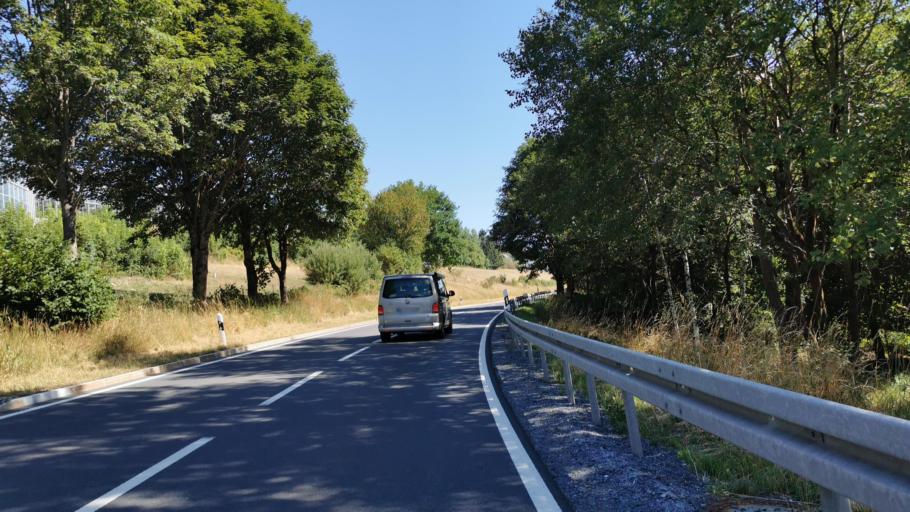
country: DE
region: Bavaria
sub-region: Upper Franconia
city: Tettau
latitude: 50.4679
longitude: 11.2763
